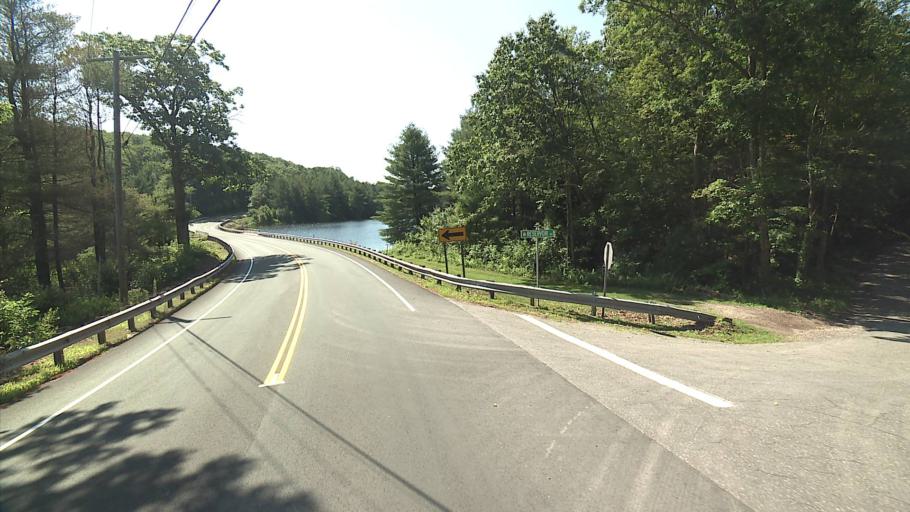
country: US
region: Connecticut
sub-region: Litchfield County
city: Northwest Harwinton
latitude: 41.7491
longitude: -73.0224
